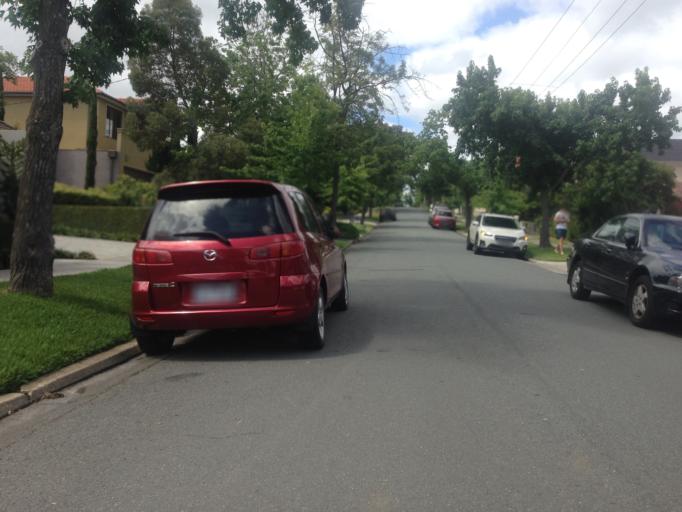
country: AU
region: Victoria
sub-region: Boroondara
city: Balwyn North
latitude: -37.7872
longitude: 145.0805
